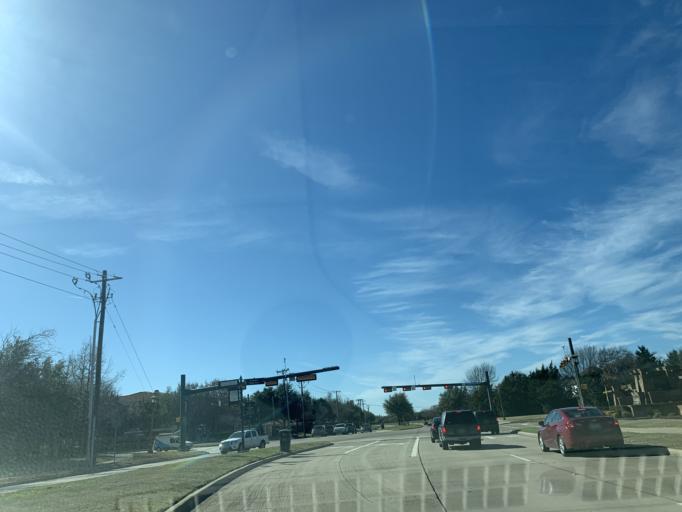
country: US
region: Texas
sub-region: Denton County
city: The Colony
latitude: 33.0841
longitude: -96.8630
